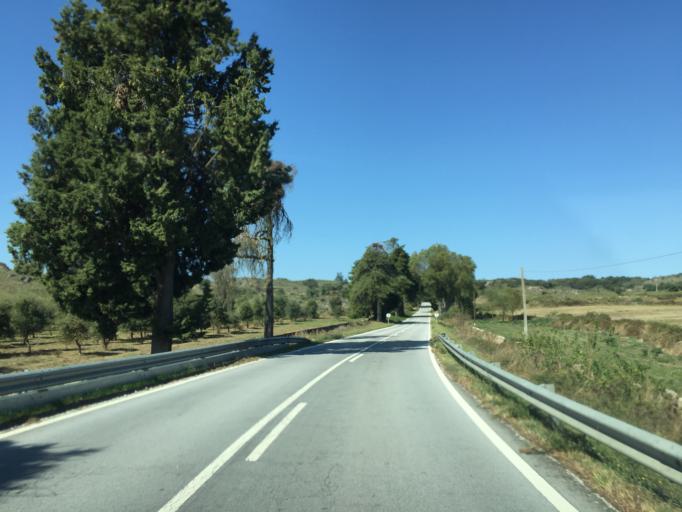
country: PT
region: Portalegre
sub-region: Portalegre
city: Alagoa
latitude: 39.4346
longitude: -7.5383
